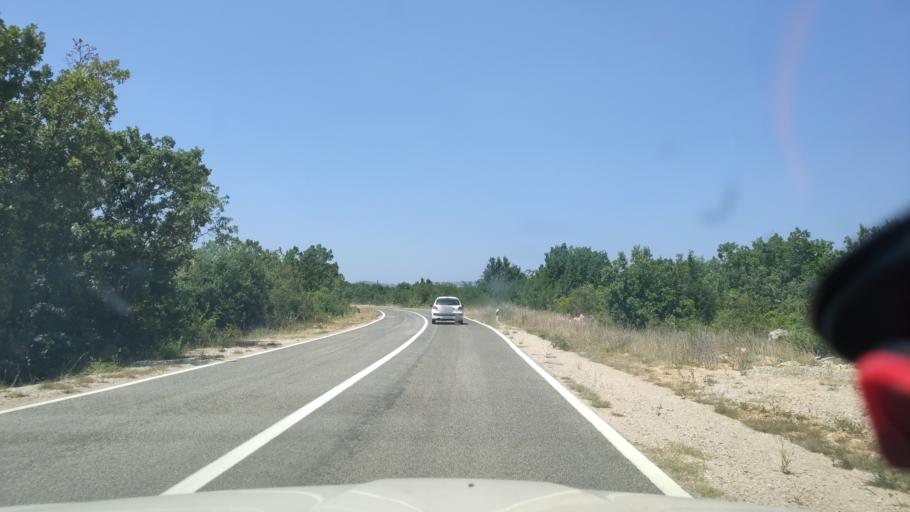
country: HR
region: Sibensko-Kniniska
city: Kistanje
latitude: 43.9703
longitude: 15.9062
